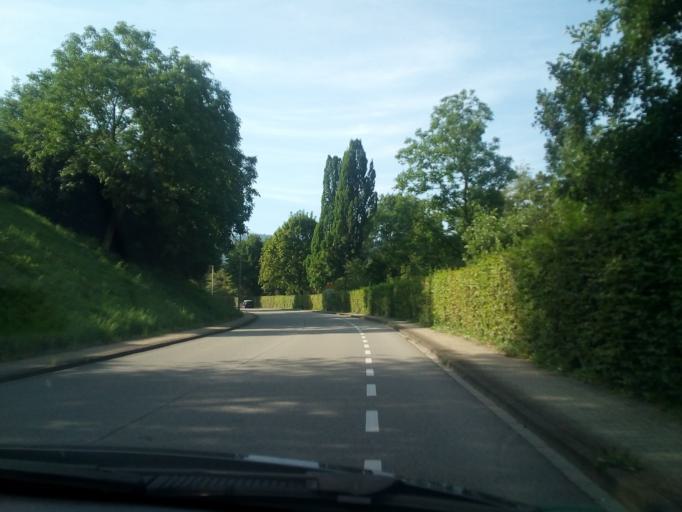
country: DE
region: Baden-Wuerttemberg
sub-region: Karlsruhe Region
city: Buhlertal
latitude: 48.6755
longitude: 8.1956
